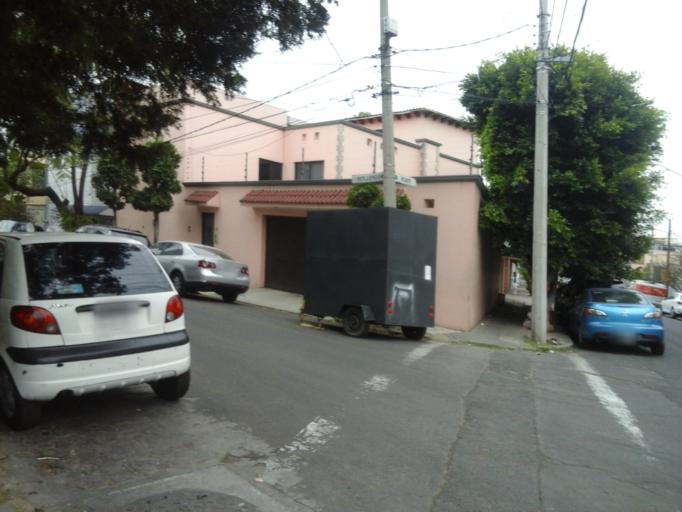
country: MX
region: Mexico
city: Colonia Lindavista
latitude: 19.4884
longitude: -99.1338
